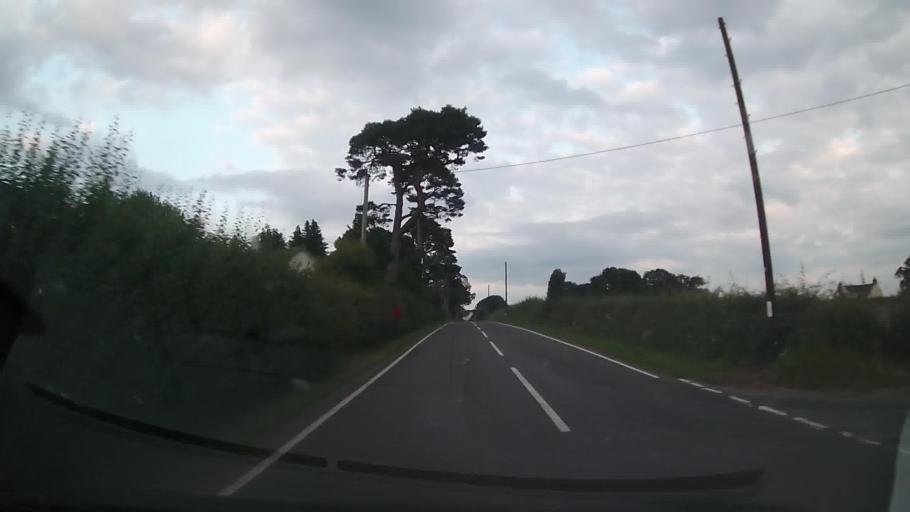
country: GB
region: England
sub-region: Shropshire
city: Petton
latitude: 52.8077
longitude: -2.8005
